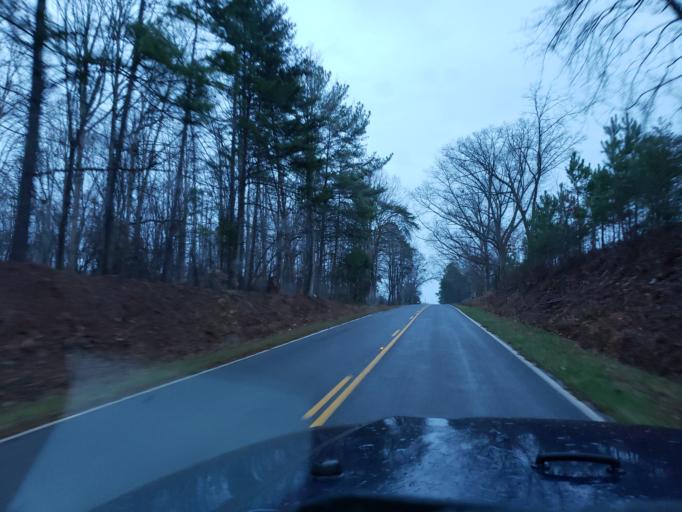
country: US
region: South Carolina
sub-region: Cherokee County
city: Blacksburg
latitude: 35.1449
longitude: -81.4422
